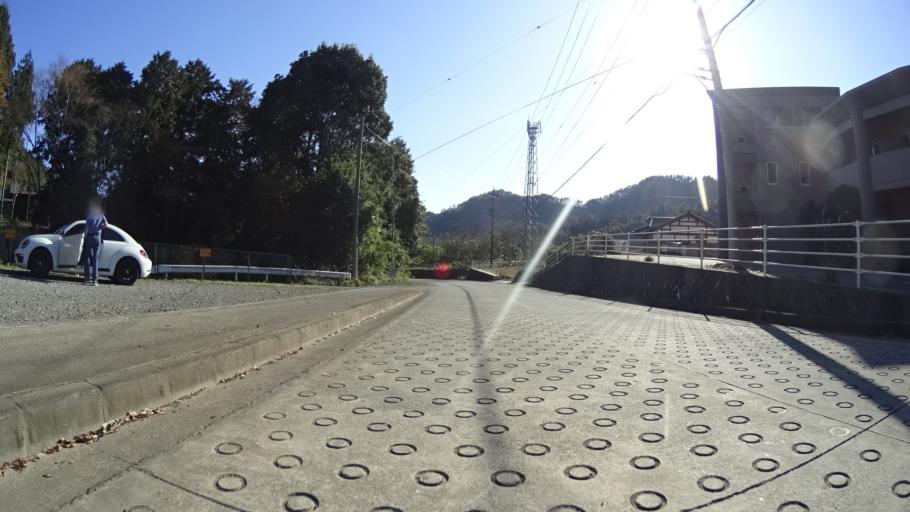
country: JP
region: Yamanashi
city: Uenohara
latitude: 35.6563
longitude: 139.1193
